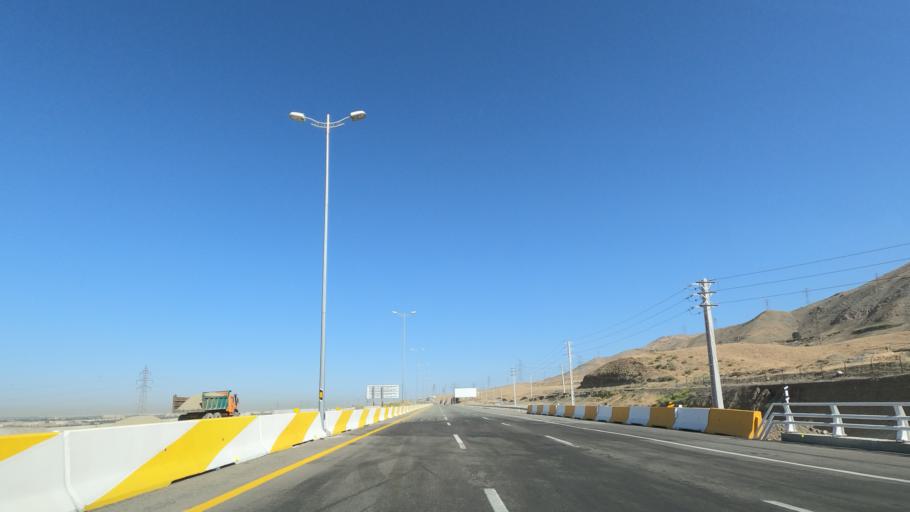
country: IR
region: Tehran
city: Shahr-e Qods
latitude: 35.7682
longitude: 51.0640
